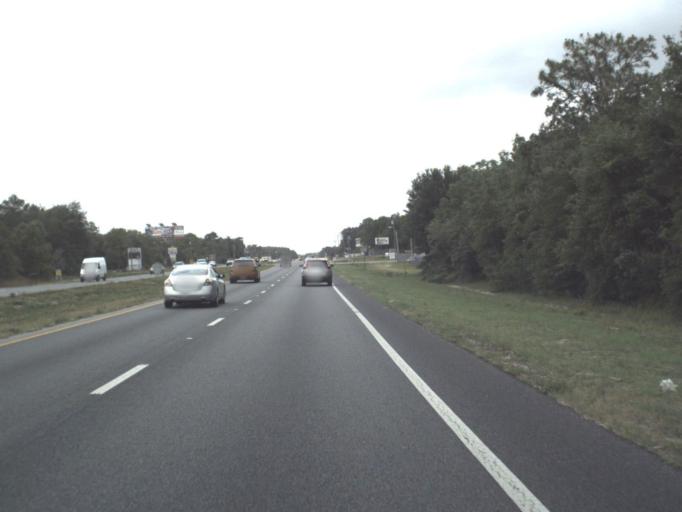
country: US
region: Florida
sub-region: Sumter County
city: The Villages
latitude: 29.0000
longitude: -82.0007
